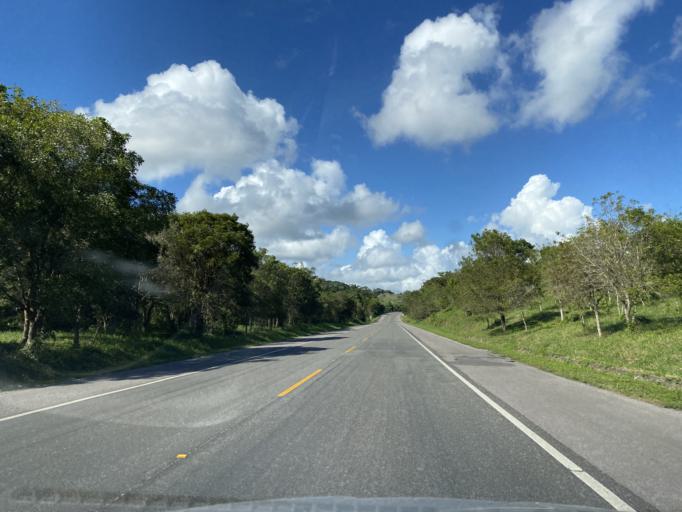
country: DO
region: Monte Plata
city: Majagual
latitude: 19.0290
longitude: -69.8247
